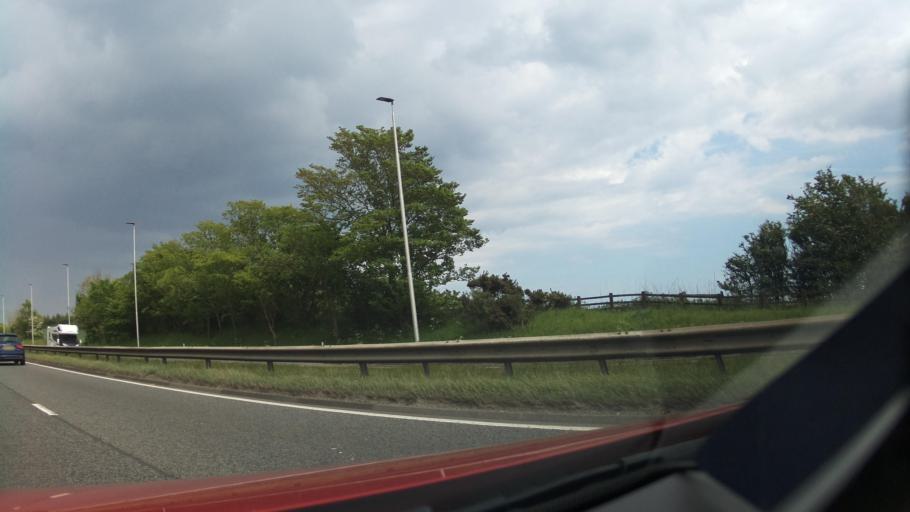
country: GB
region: England
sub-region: County Durham
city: Hawthorn
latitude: 54.7973
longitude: -1.3632
